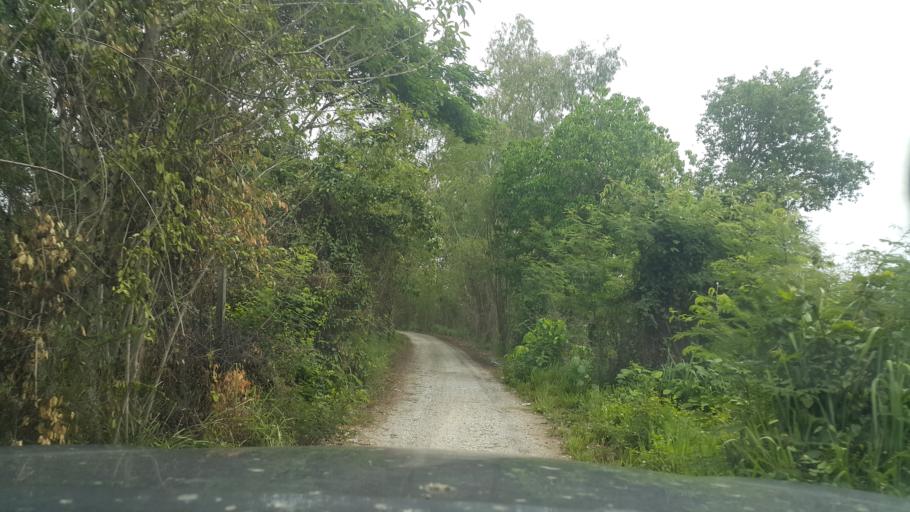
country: TH
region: Chiang Mai
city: Hang Dong
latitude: 18.6790
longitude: 98.8924
